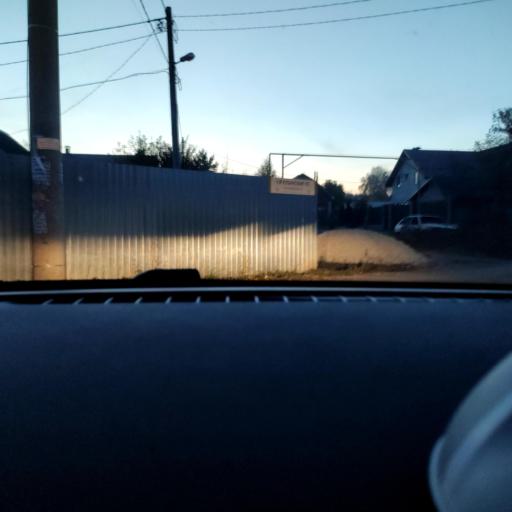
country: RU
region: Samara
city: Petra-Dubrava
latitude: 53.2996
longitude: 50.3084
